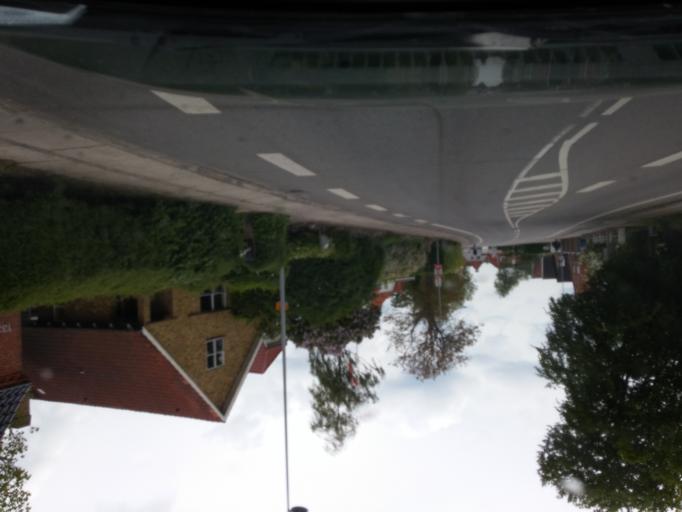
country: DK
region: South Denmark
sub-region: Odense Kommune
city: Odense
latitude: 55.4047
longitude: 10.3546
